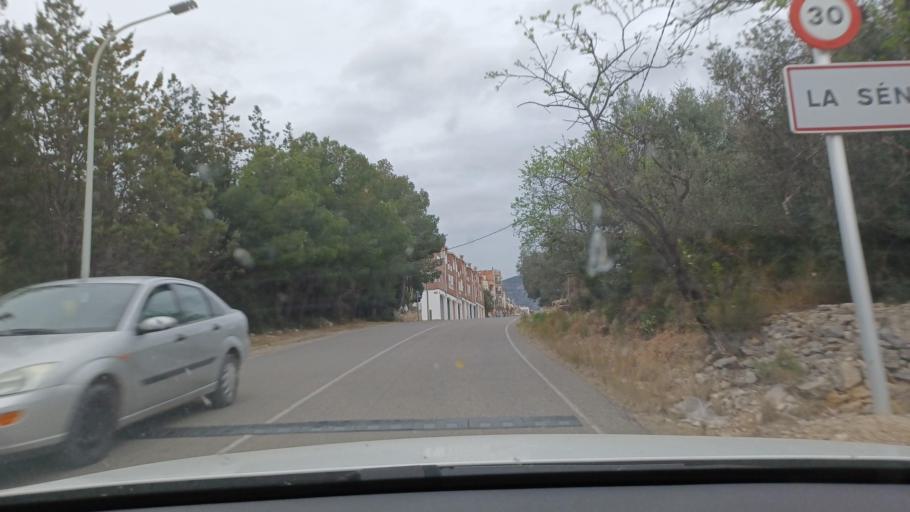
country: ES
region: Valencia
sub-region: Provincia de Castello
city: Rosell
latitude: 40.6309
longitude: 0.2880
